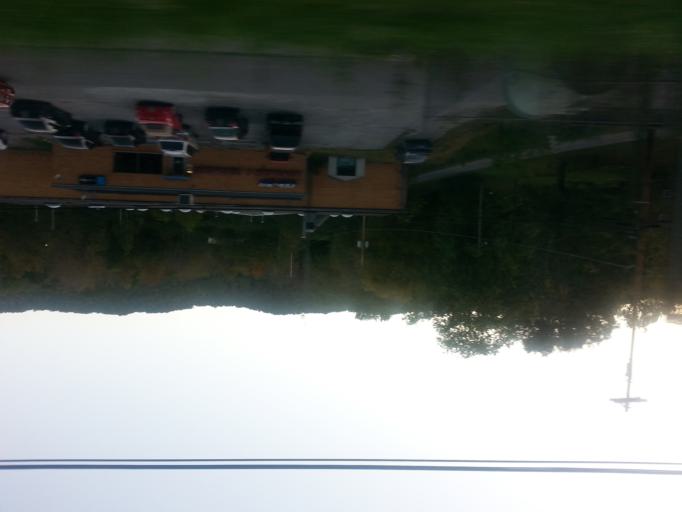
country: US
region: Tennessee
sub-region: Campbell County
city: Hunter
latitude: 36.3608
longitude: -84.1421
